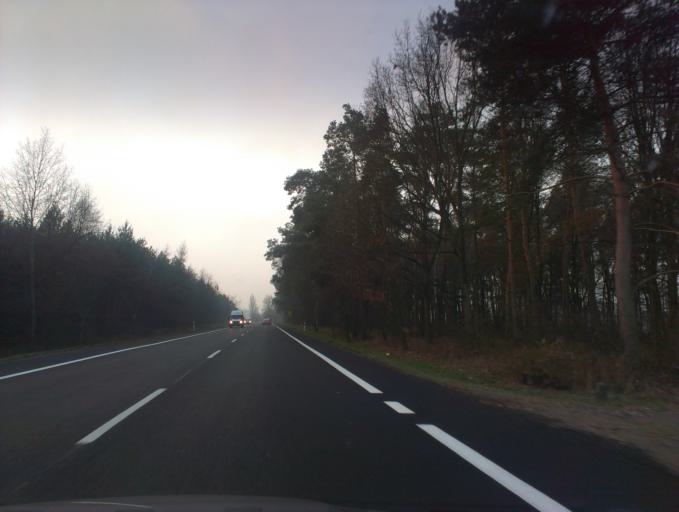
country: PL
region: Greater Poland Voivodeship
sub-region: Powiat obornicki
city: Rogozno
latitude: 52.8065
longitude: 16.9778
